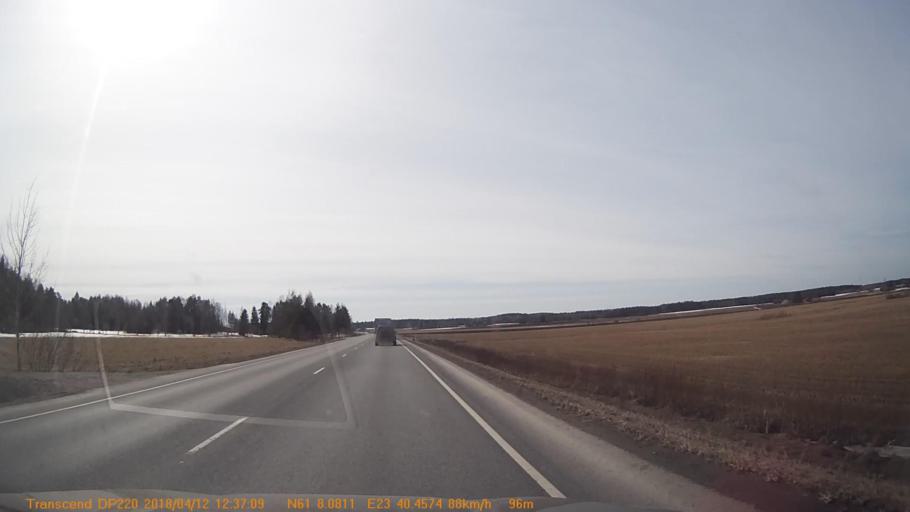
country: FI
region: Pirkanmaa
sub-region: Etelae-Pirkanmaa
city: Kylmaekoski
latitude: 61.1348
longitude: 23.6744
